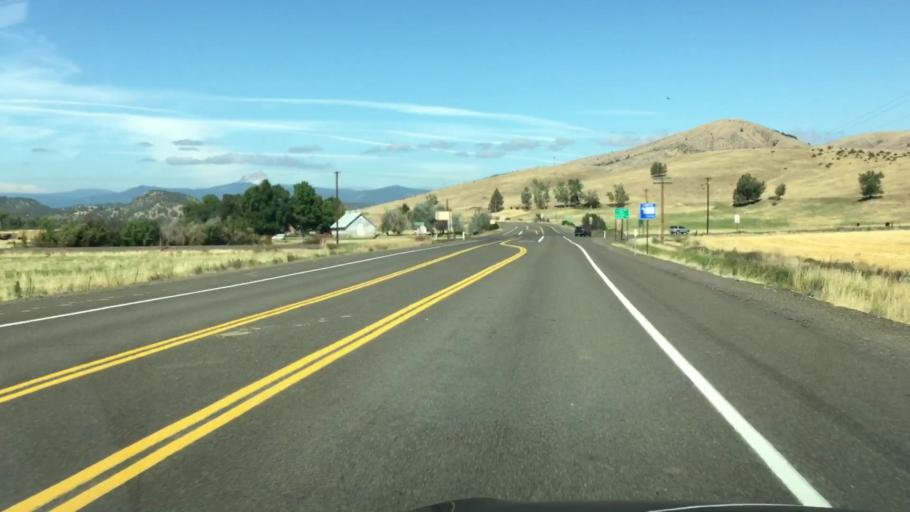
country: US
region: Oregon
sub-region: Wasco County
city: The Dalles
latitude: 45.2515
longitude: -121.1728
